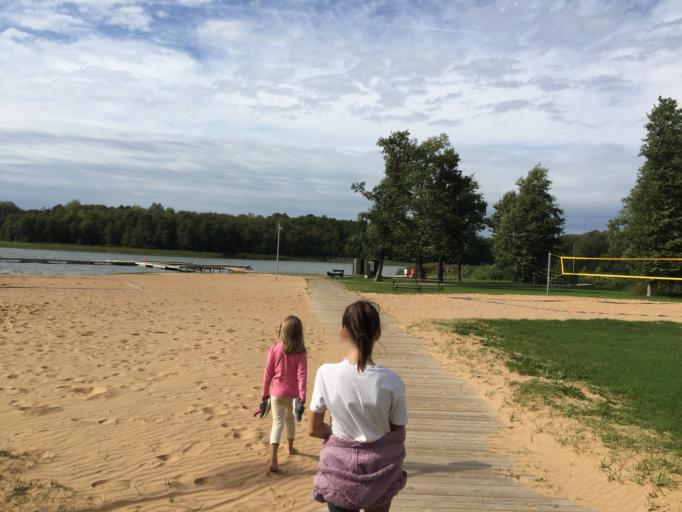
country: LV
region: Limbazu Rajons
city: Limbazi
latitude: 57.5035
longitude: 24.7030
